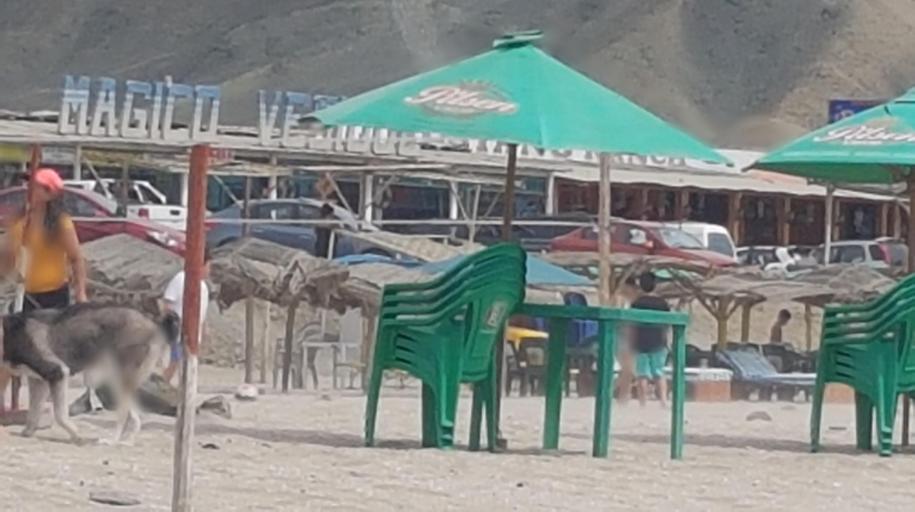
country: PE
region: Ancash
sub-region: Provincia de Santa
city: Buenos Aires
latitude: -9.1522
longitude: -78.5064
